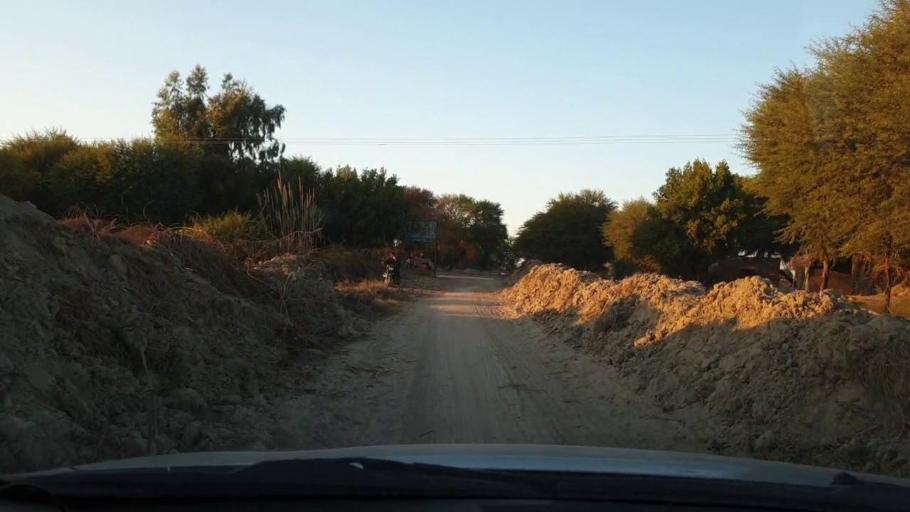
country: PK
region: Sindh
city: Jhol
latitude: 25.8975
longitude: 68.8869
